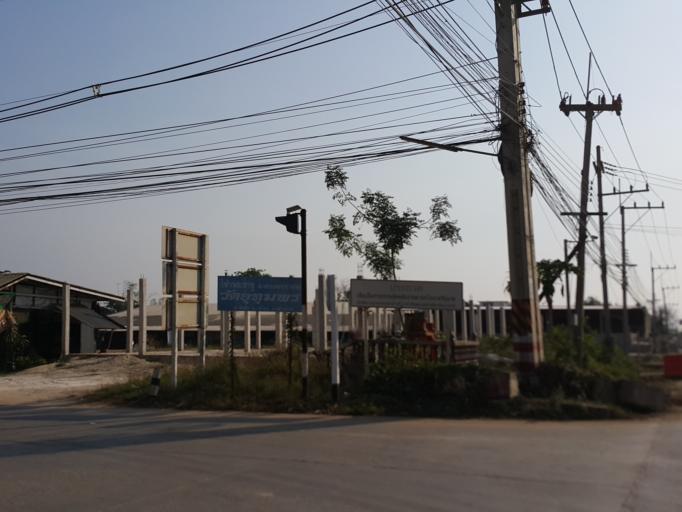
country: TH
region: Lampang
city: Lampang
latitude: 18.3436
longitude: 99.5358
